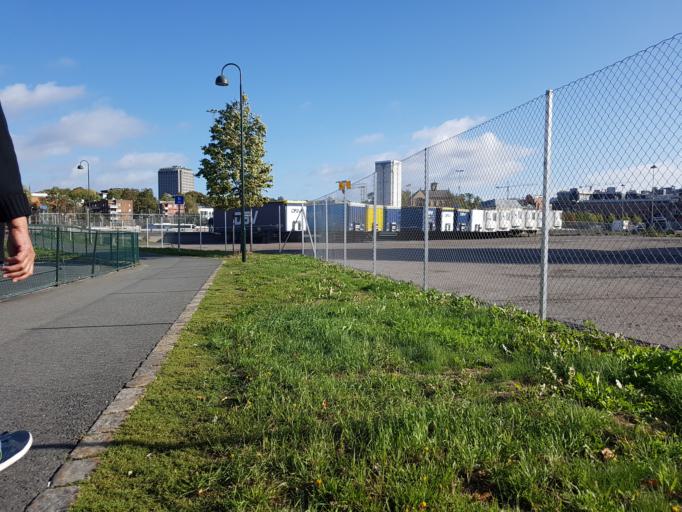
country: NO
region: Oslo
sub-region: Oslo
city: Oslo
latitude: 59.9090
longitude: 10.7143
